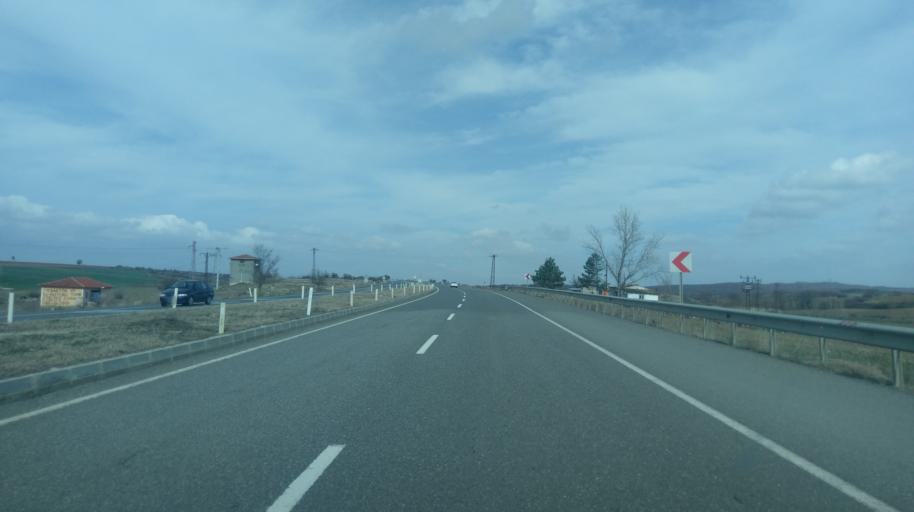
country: TR
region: Edirne
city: Hamidiye
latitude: 41.1144
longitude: 26.6502
